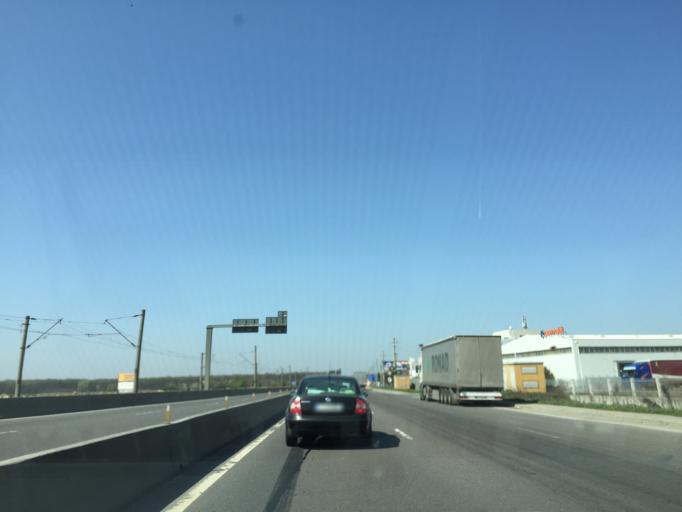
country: RO
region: Ilfov
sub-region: Comuna Tunari
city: Tunari
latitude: 44.5363
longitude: 26.1391
